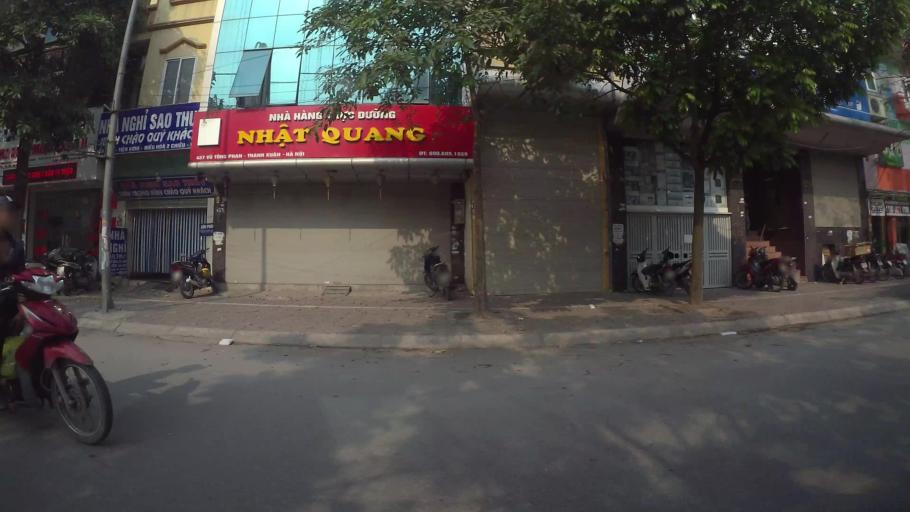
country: VN
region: Ha Noi
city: Thanh Xuan
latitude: 20.9873
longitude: 105.8137
